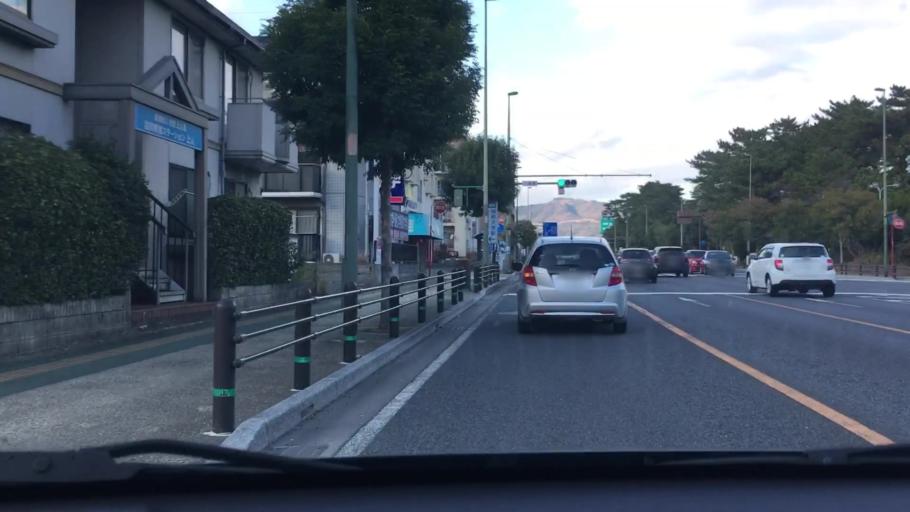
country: JP
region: Oita
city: Beppu
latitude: 33.3123
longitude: 131.5009
